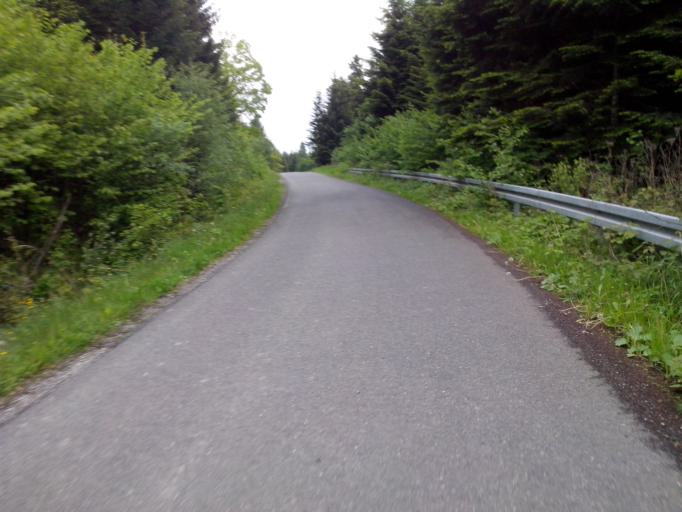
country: PL
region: Subcarpathian Voivodeship
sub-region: Powiat strzyzowski
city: Wysoka Strzyzowska
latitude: 49.8215
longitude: 21.7853
